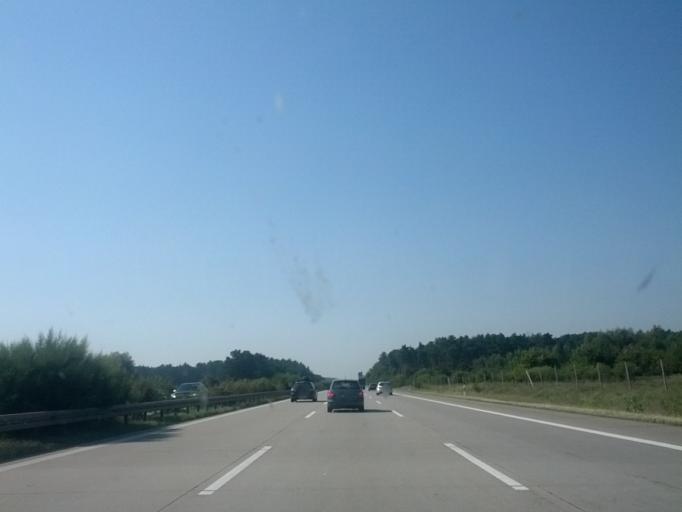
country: DE
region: Brandenburg
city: Linthe
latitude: 52.1478
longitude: 12.7696
